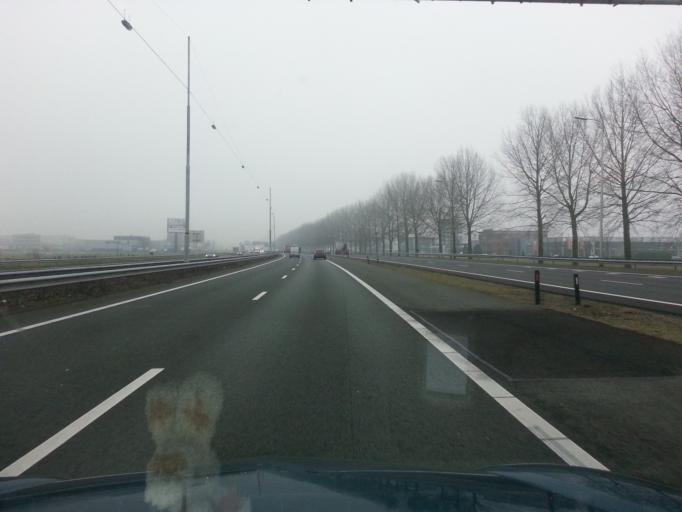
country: NL
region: Gelderland
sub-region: Gemeente Duiven
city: Duiven
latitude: 51.9665
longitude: 6.0030
